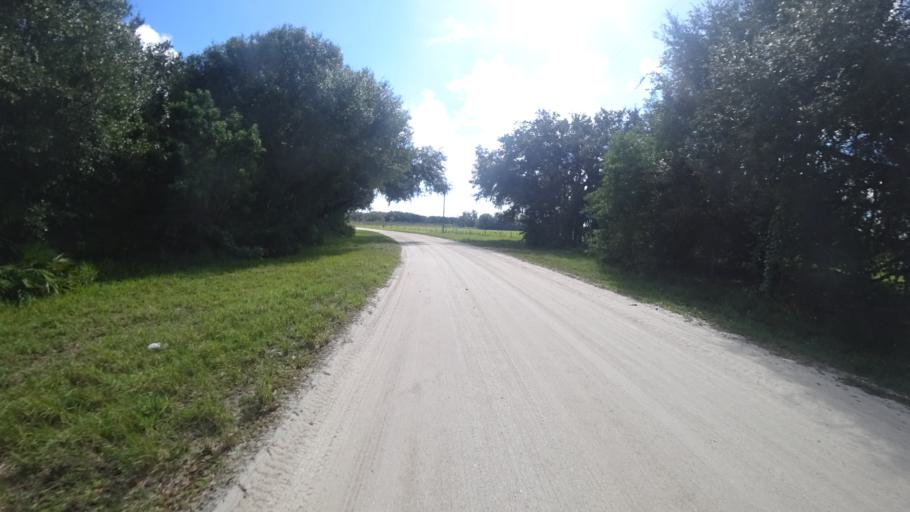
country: US
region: Florida
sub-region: DeSoto County
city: Arcadia
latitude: 27.3558
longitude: -82.1275
